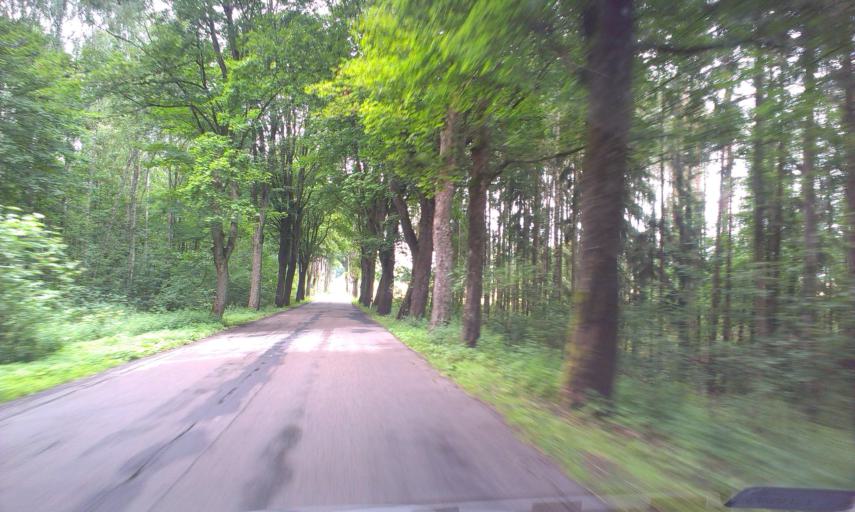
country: PL
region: West Pomeranian Voivodeship
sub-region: Powiat szczecinecki
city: Barwice
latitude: 53.6713
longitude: 16.3435
